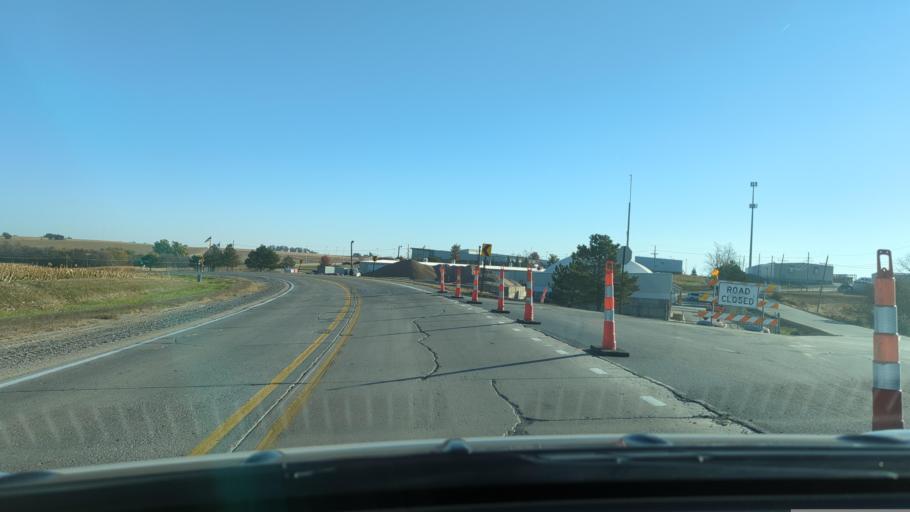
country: US
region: Nebraska
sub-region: Sarpy County
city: Papillion
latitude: 41.0886
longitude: -96.0456
